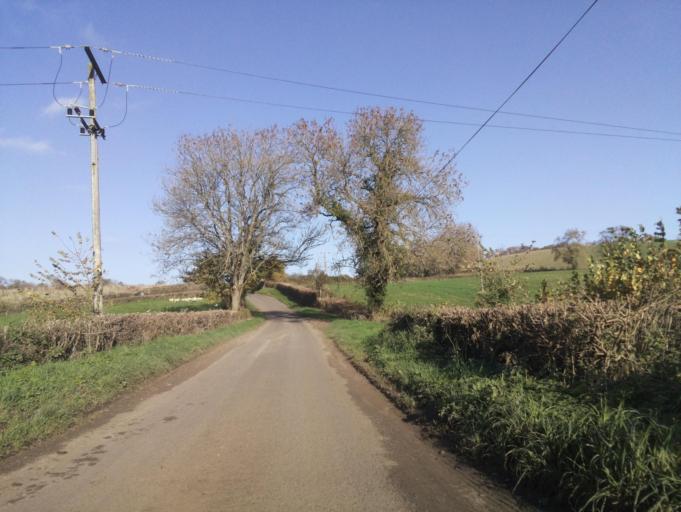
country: GB
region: England
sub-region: Somerset
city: Castle Cary
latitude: 51.0612
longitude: -2.4781
